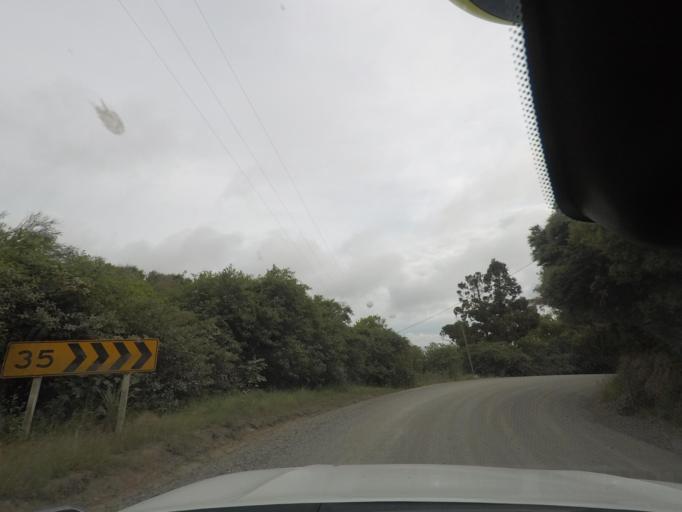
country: NZ
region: Auckland
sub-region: Auckland
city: Parakai
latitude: -36.4835
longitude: 174.2517
